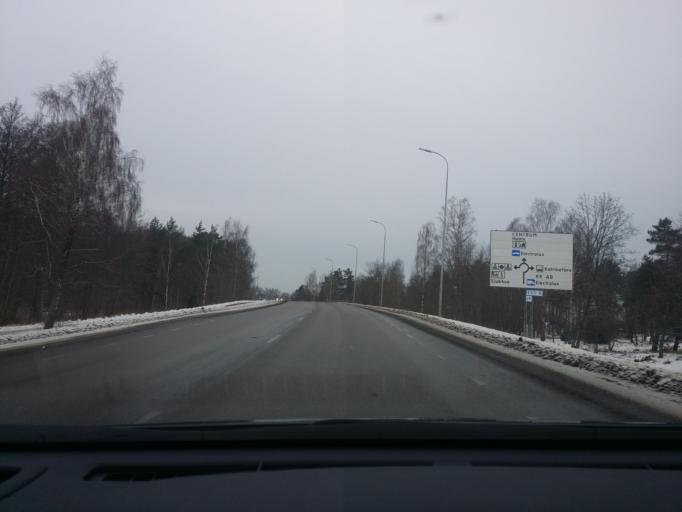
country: SE
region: Vaestra Goetaland
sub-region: Mariestads Kommun
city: Mariestad
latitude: 58.6890
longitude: 13.8188
